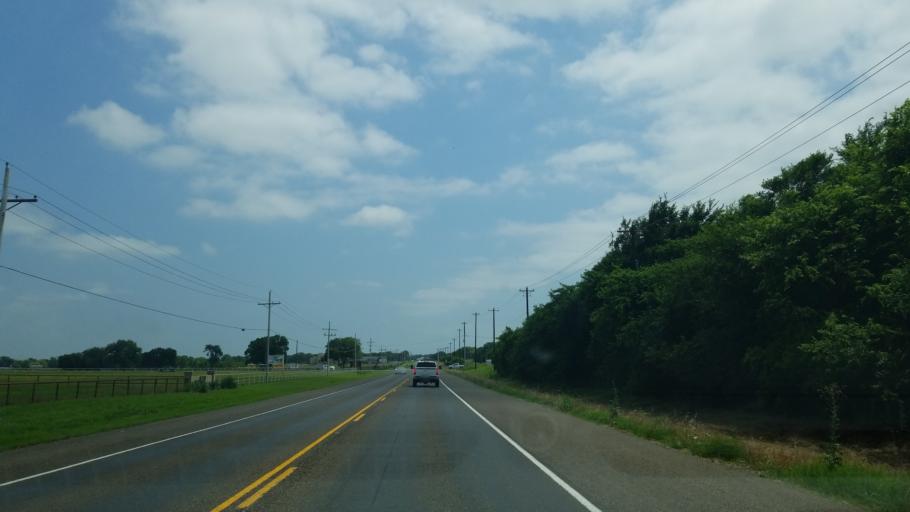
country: US
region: Texas
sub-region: Denton County
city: Aubrey
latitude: 33.3486
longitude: -96.9678
